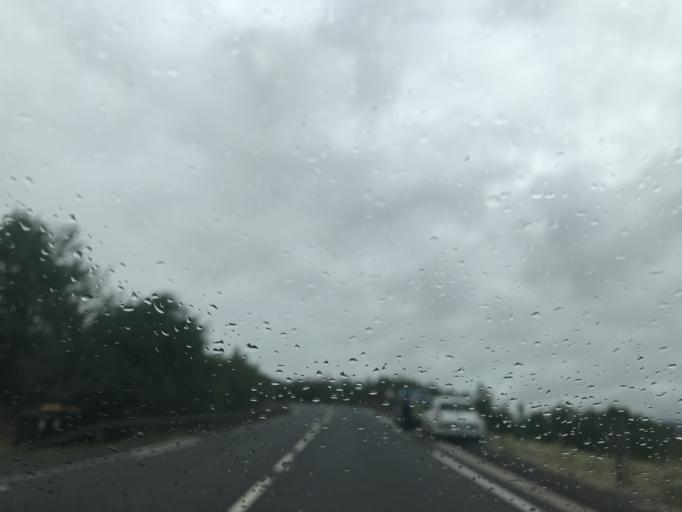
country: FR
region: Auvergne
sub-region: Departement de la Haute-Loire
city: Polignac
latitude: 45.0649
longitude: 3.8524
